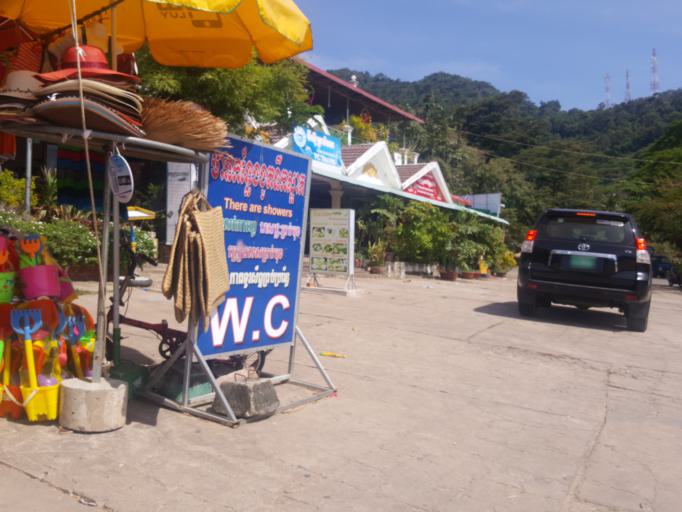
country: KH
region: Kep
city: Krong Kep
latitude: 10.4801
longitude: 104.2933
